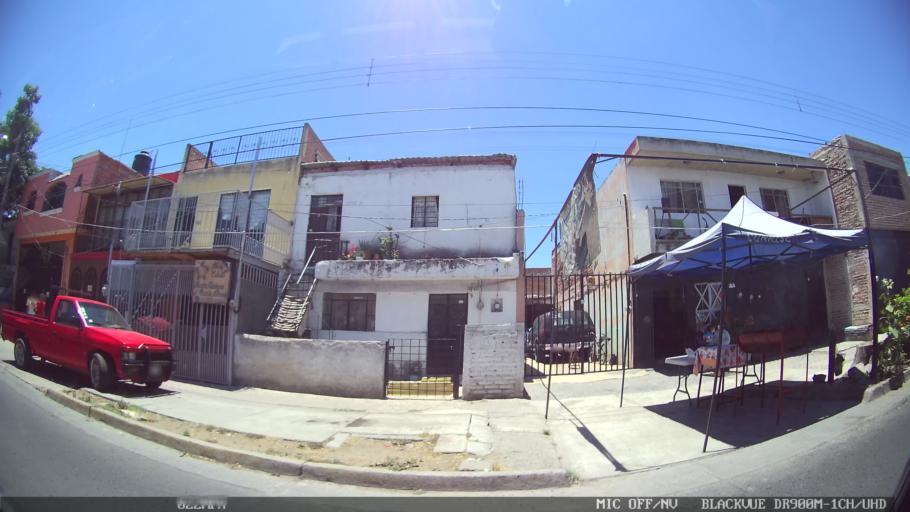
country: MX
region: Jalisco
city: Tlaquepaque
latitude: 20.6610
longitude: -103.2853
